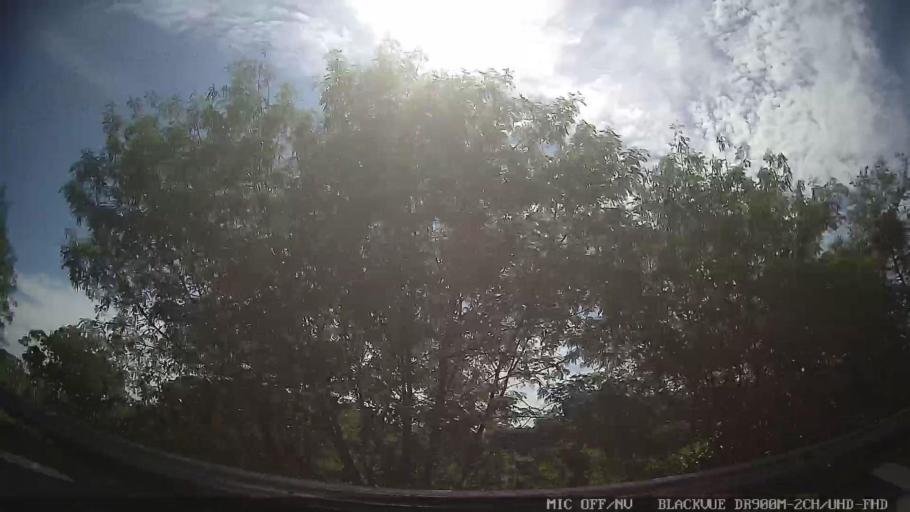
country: BR
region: Sao Paulo
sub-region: Porto Feliz
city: Porto Feliz
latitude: -23.2173
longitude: -47.5710
